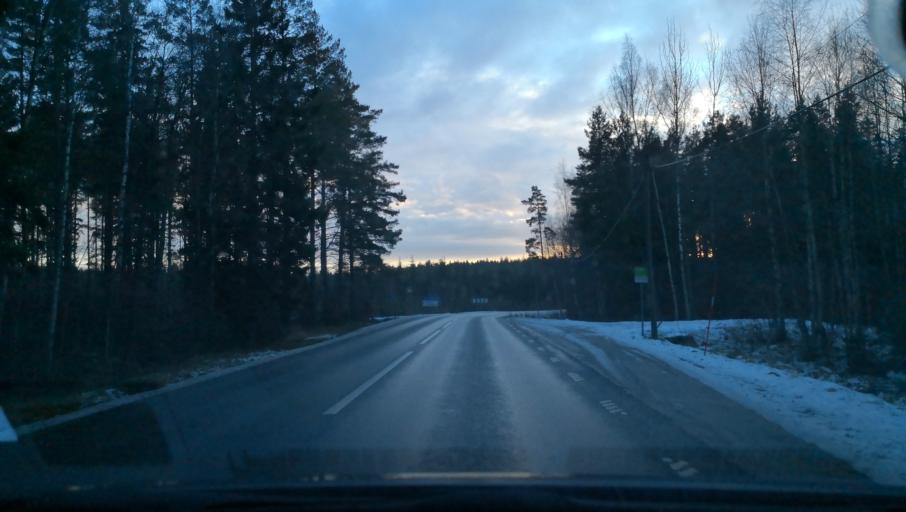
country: SE
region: Soedermanland
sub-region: Eskilstuna Kommun
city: Skogstorp
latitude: 59.2558
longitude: 16.3605
